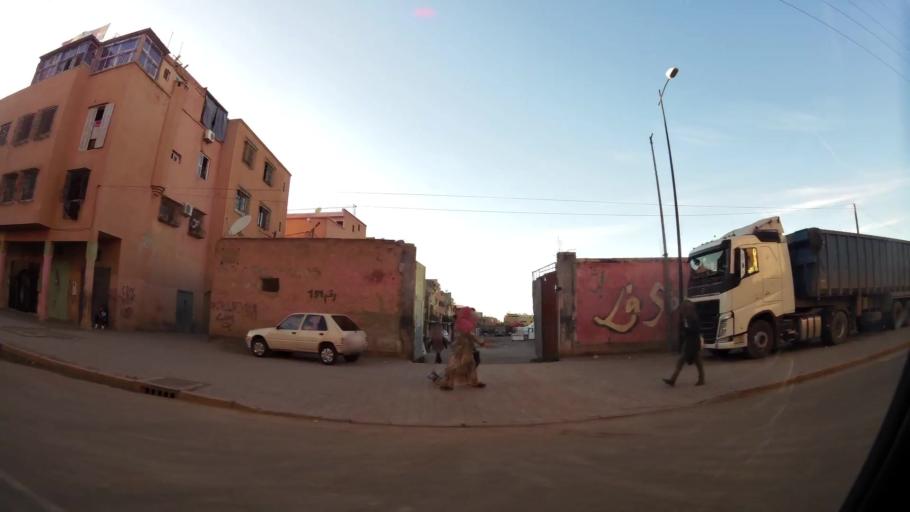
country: MA
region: Marrakech-Tensift-Al Haouz
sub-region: Marrakech
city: Marrakesh
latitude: 31.6189
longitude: -8.0553
